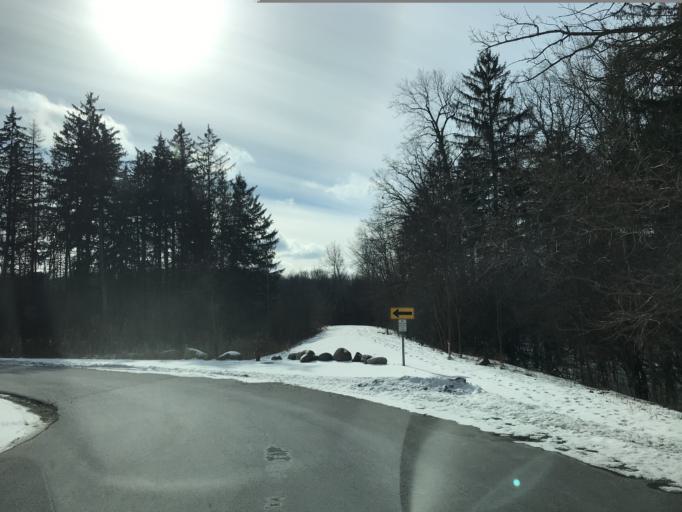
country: US
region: Michigan
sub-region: Washtenaw County
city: Ypsilanti
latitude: 42.2650
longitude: -83.6700
